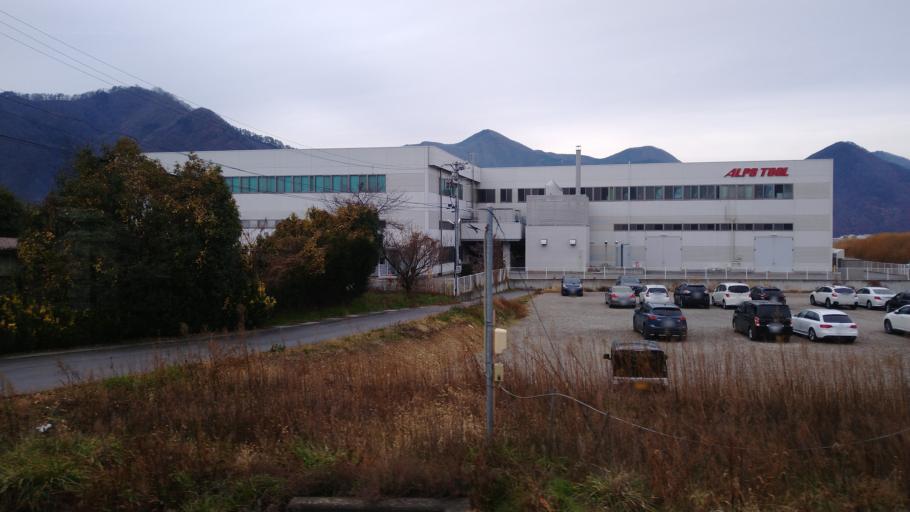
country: JP
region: Nagano
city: Ueda
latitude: 36.4435
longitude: 138.1876
